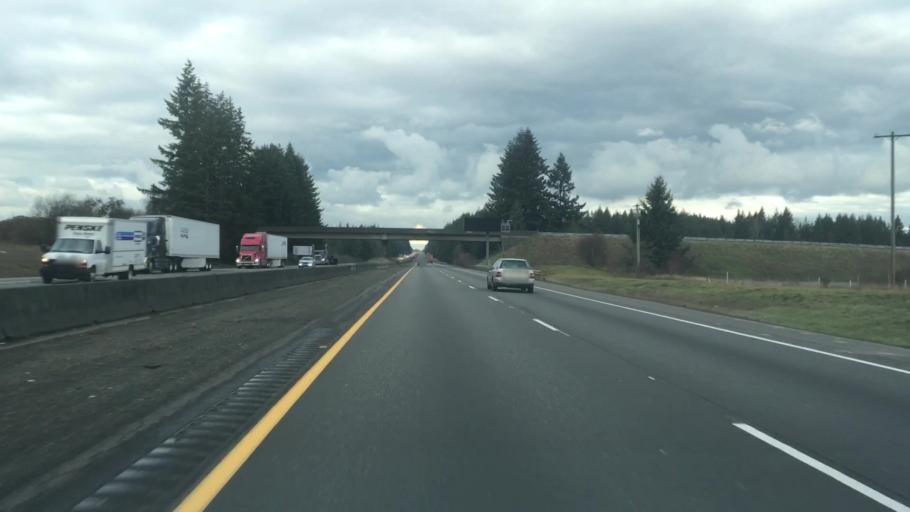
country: US
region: Washington
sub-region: Lewis County
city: Napavine
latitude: 46.5165
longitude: -122.8766
